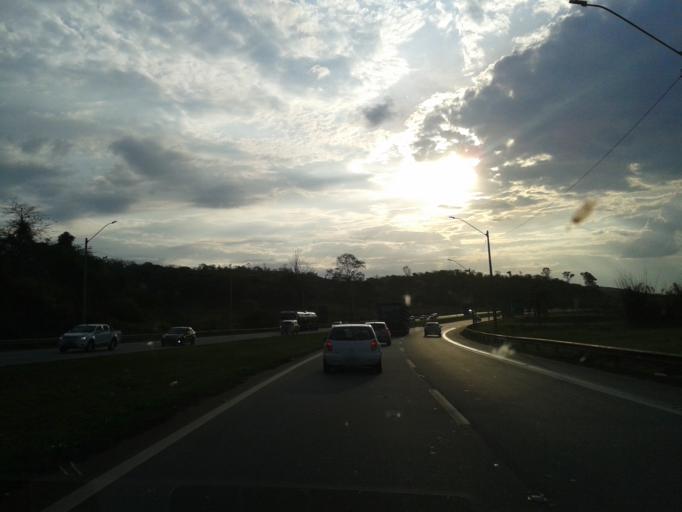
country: BR
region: Minas Gerais
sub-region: Betim
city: Betim
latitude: -19.9899
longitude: -44.1912
